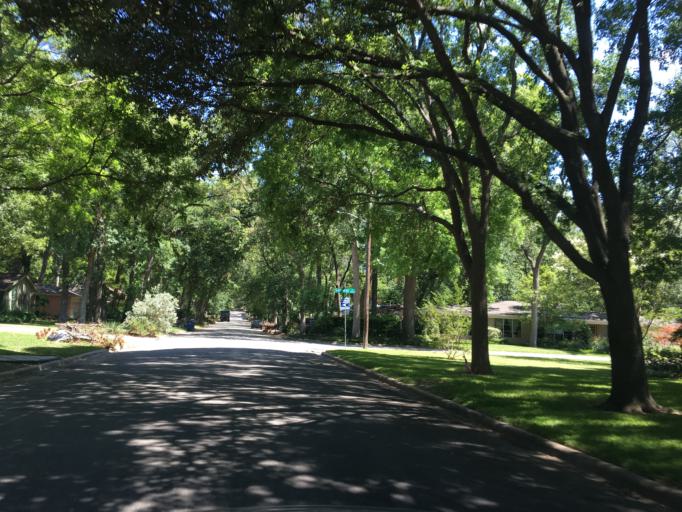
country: US
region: Texas
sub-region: Dallas County
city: Garland
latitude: 32.8460
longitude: -96.6992
